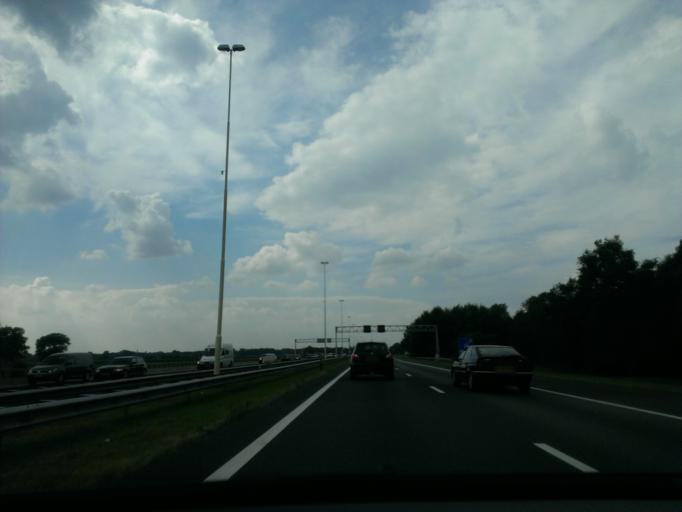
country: NL
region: Utrecht
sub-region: Gemeente Baarn
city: Baarn
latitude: 52.2146
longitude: 5.3299
